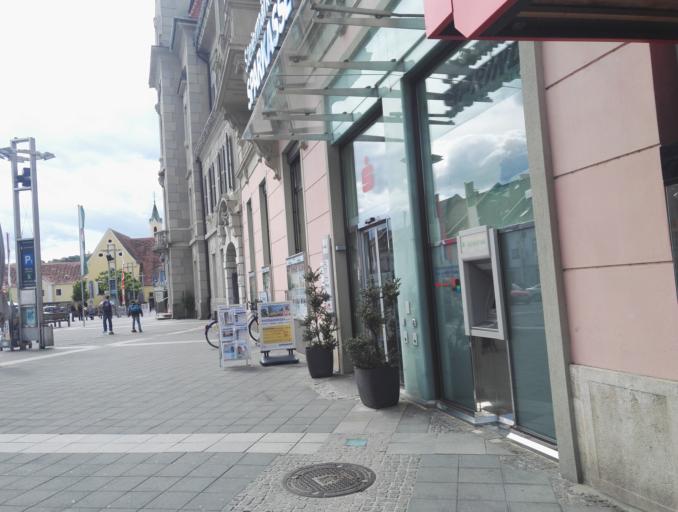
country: AT
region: Styria
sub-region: Politischer Bezirk Leibnitz
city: Leibnitz
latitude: 46.7816
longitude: 15.5385
